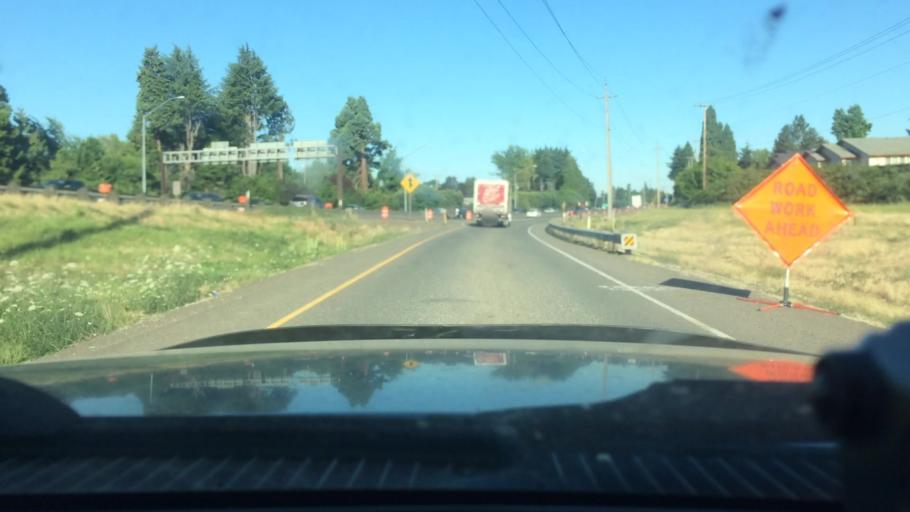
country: US
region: Oregon
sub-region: Lane County
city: Eugene
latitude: 44.0974
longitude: -123.1310
